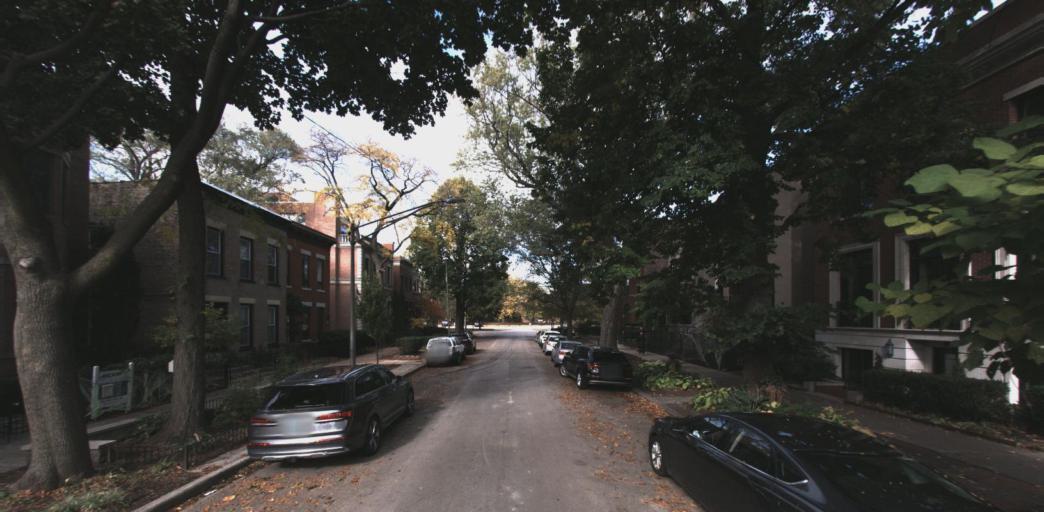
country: US
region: Illinois
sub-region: Cook County
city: Chicago
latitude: 41.9229
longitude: -87.6596
